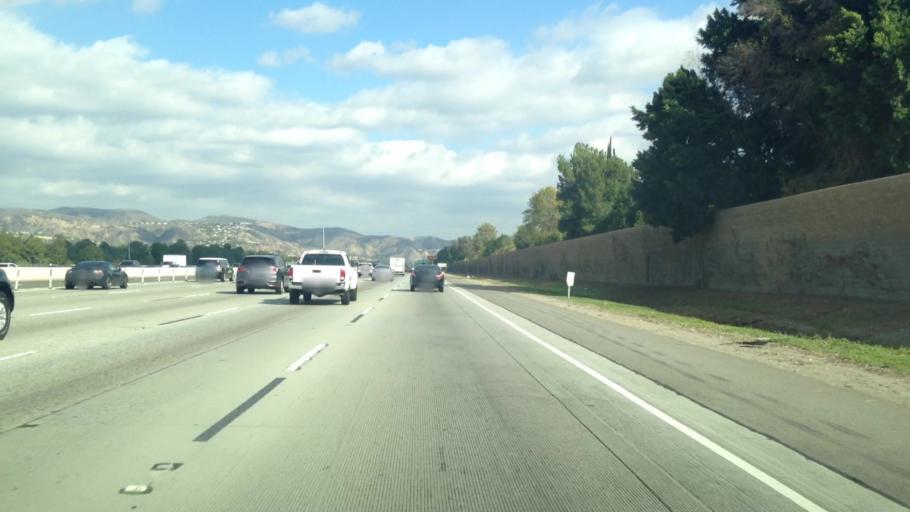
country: US
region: California
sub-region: Orange County
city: Yorba Linda
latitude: 33.8588
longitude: -117.7799
